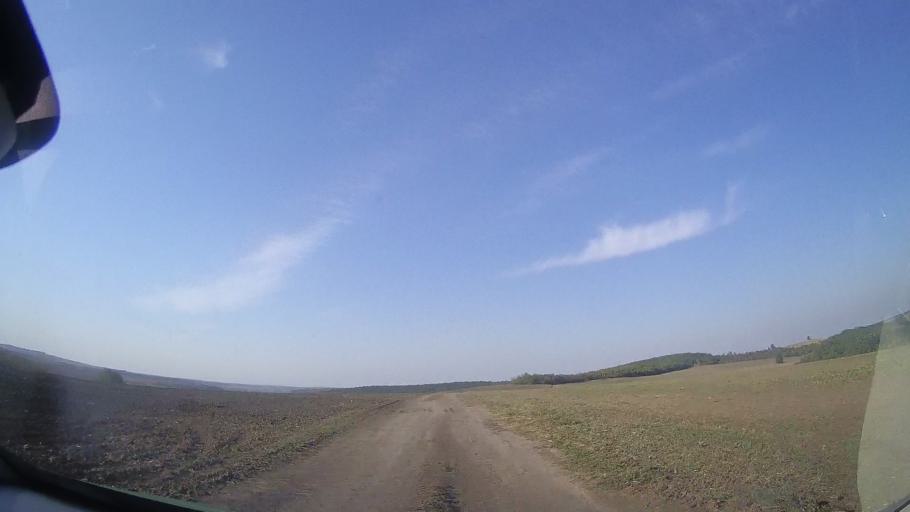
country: RO
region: Timis
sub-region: Comuna Bogda
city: Bogda
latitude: 45.9109
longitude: 21.6016
